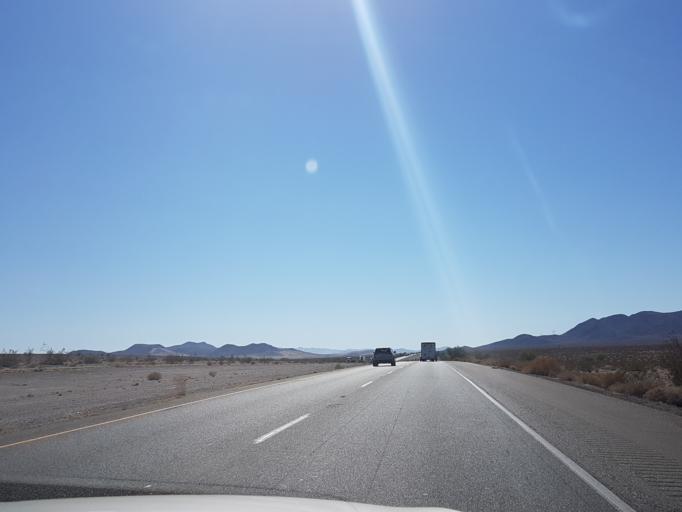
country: US
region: California
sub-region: San Bernardino County
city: Fort Irwin
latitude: 35.1832
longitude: -116.1663
